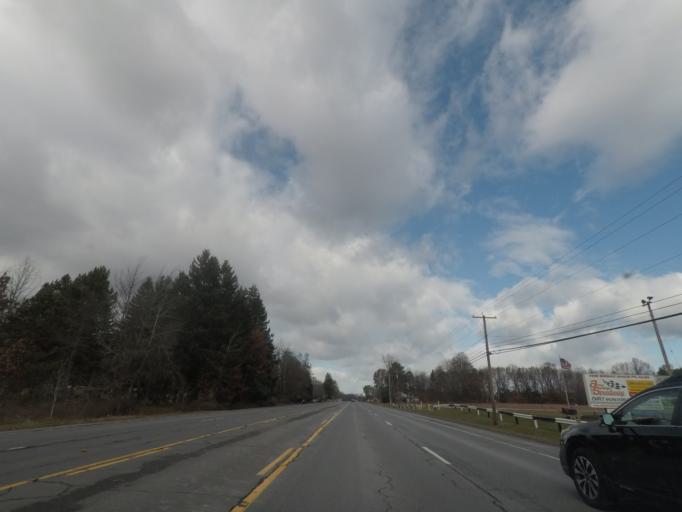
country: US
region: New York
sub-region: Saratoga County
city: Ballston Spa
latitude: 42.9886
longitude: -73.7881
